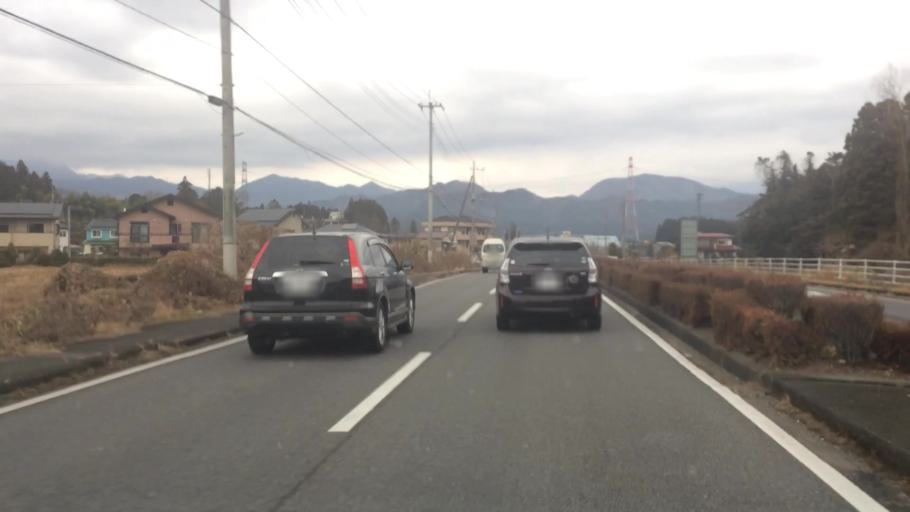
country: JP
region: Tochigi
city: Imaichi
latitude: 36.7587
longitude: 139.7164
